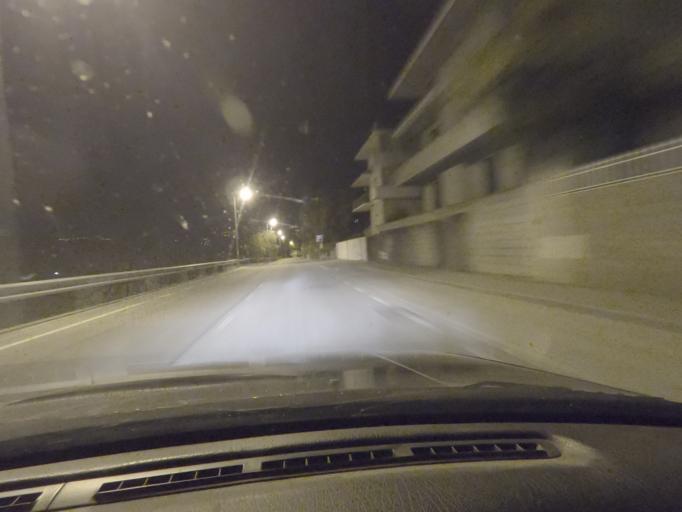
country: PT
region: Vila Real
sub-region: Peso da Regua
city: Godim
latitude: 41.1745
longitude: -7.7959
